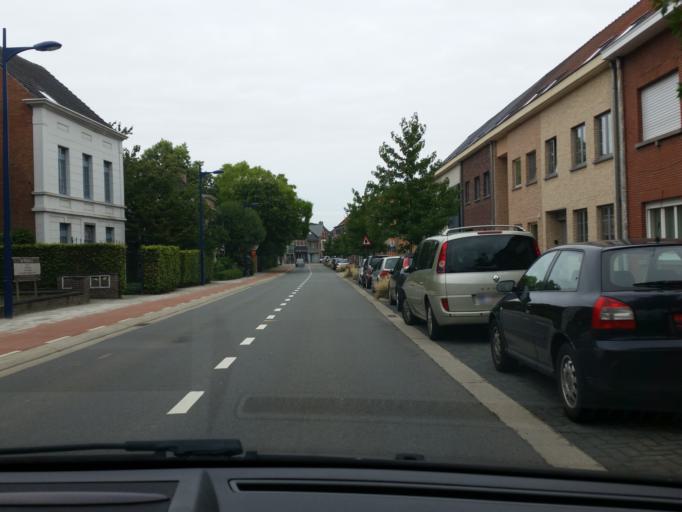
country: BE
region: Flanders
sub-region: Provincie Antwerpen
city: Kontich
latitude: 51.1309
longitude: 4.4485
